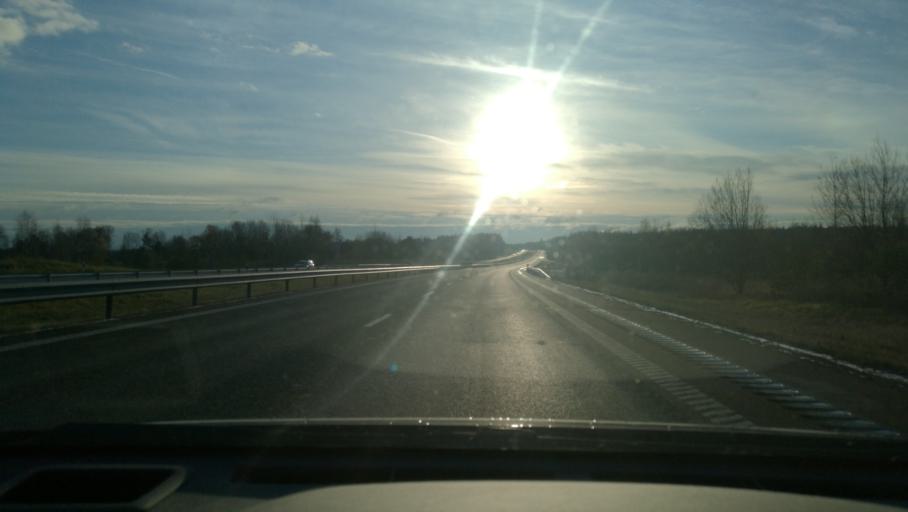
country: SE
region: Vaestmanland
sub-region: Kopings Kommun
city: Koping
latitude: 59.5017
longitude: 15.9343
